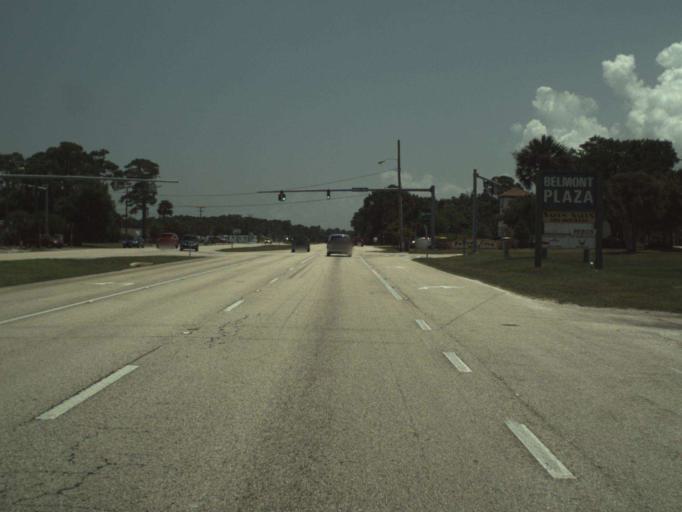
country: US
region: Florida
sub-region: Volusia County
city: Edgewater
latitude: 28.9668
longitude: -80.8925
